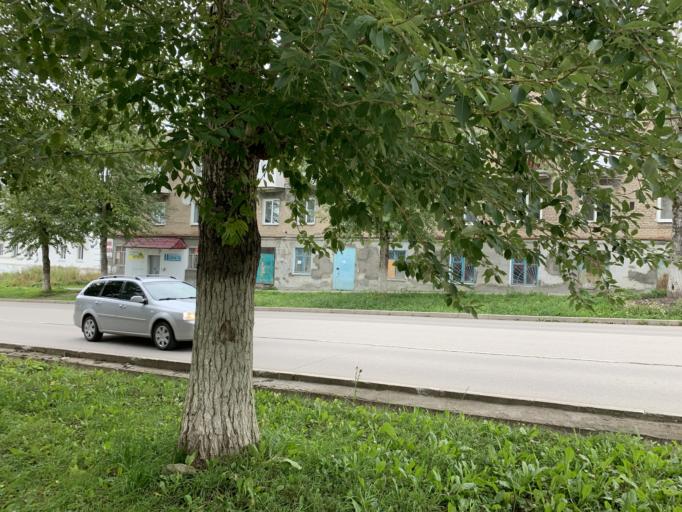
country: RU
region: Perm
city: Gubakha
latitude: 58.8433
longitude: 57.5499
